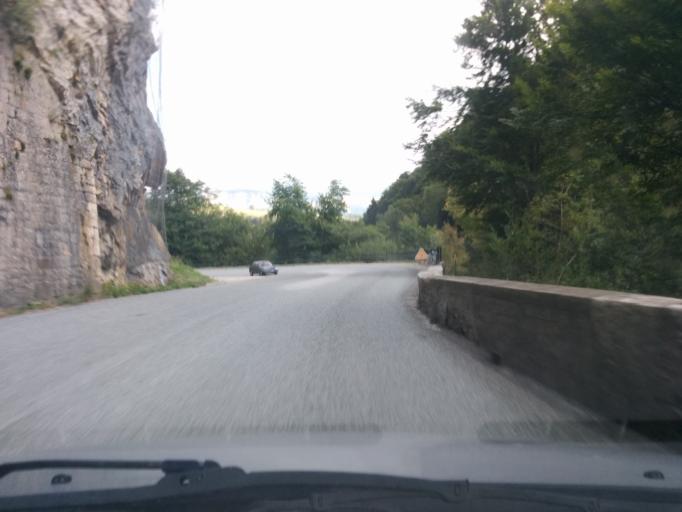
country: FR
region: Rhone-Alpes
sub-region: Departement de la Savoie
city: Saint-Beron
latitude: 45.4762
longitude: 5.7322
